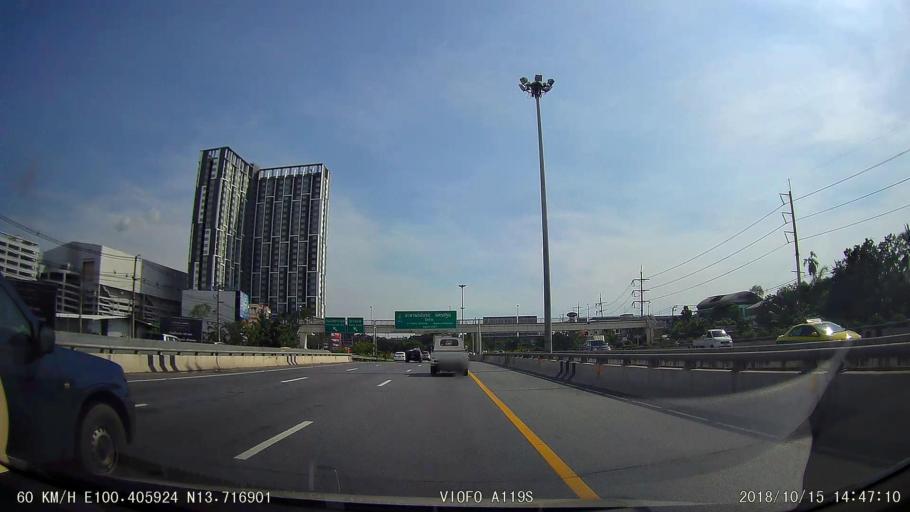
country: TH
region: Bangkok
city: Bang Khae
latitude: 13.7166
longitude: 100.4059
